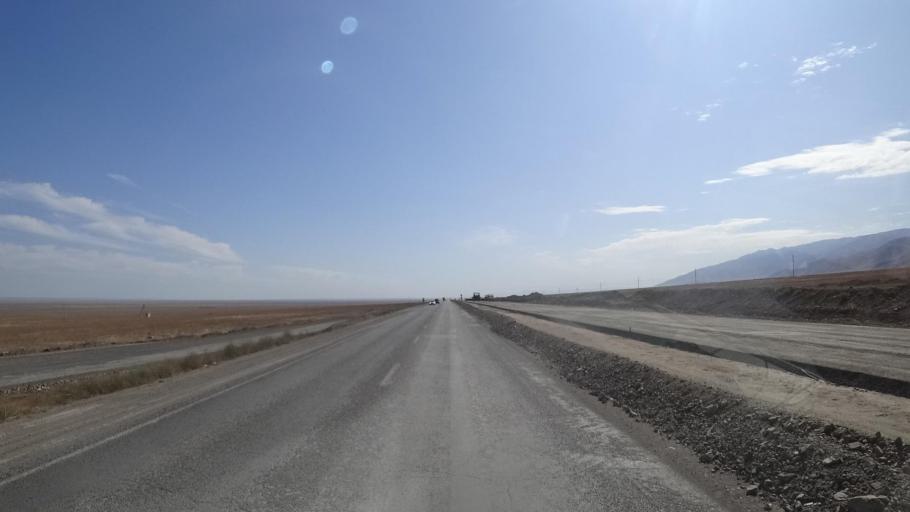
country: KG
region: Chuy
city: Ivanovka
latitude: 43.3830
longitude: 75.1865
